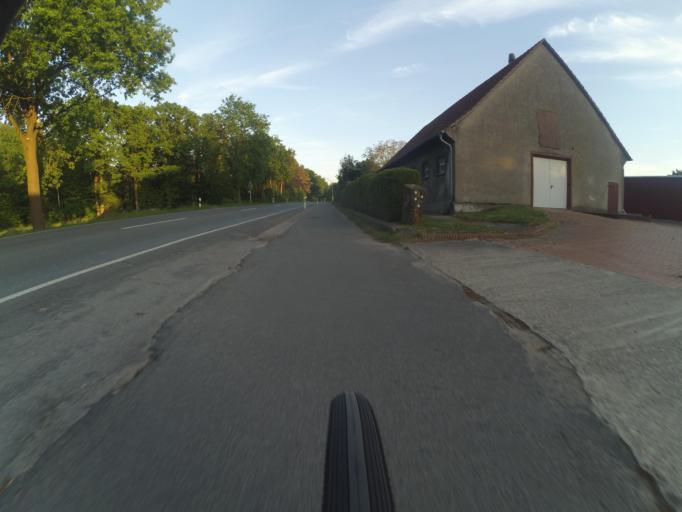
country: DE
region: North Rhine-Westphalia
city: Ibbenburen
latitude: 52.3191
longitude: 7.6727
